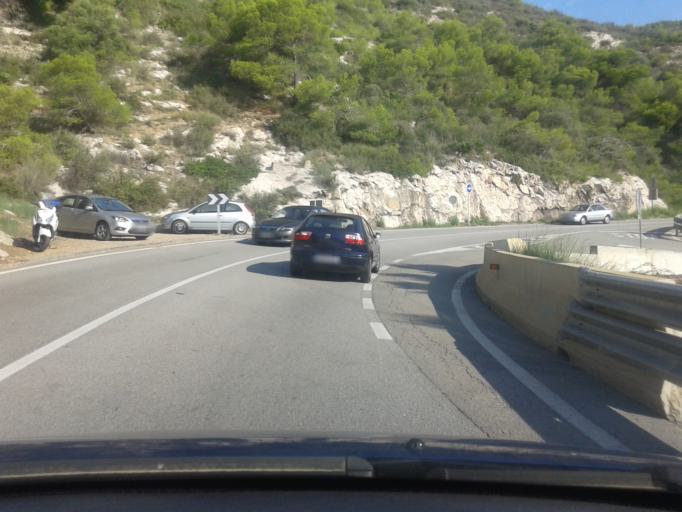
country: ES
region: Catalonia
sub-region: Provincia de Barcelona
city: Sitges
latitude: 41.2436
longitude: 1.8672
